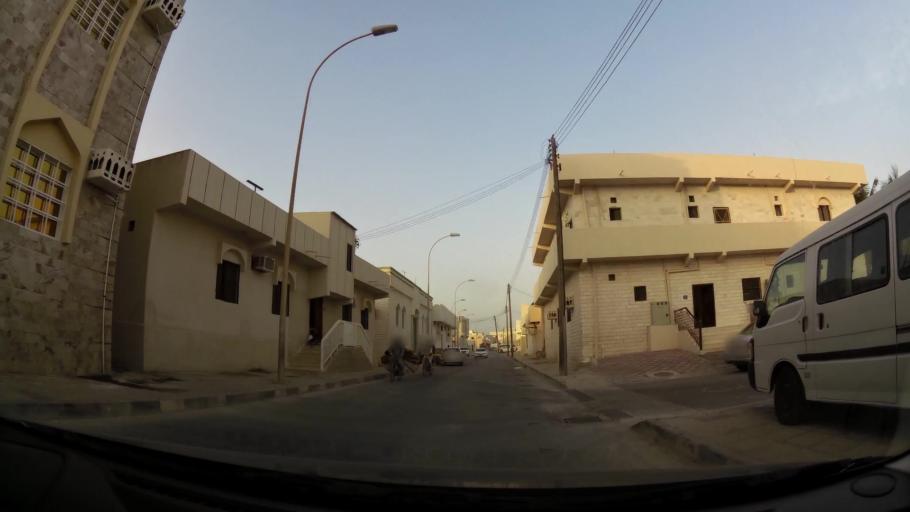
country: OM
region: Zufar
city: Salalah
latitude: 17.0189
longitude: 54.1178
